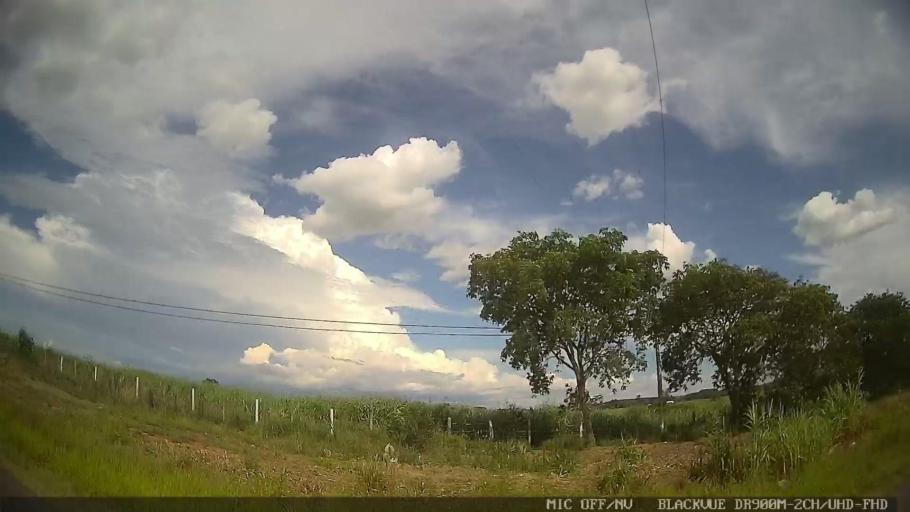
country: BR
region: Sao Paulo
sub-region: Conchas
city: Conchas
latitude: -23.0517
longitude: -47.9589
